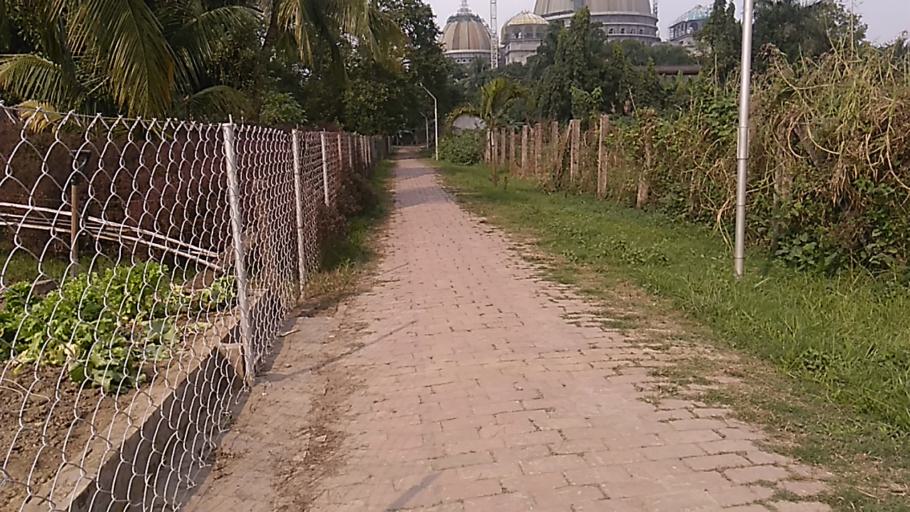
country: IN
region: West Bengal
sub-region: Nadia
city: Navadwip
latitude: 23.4215
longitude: 88.3890
